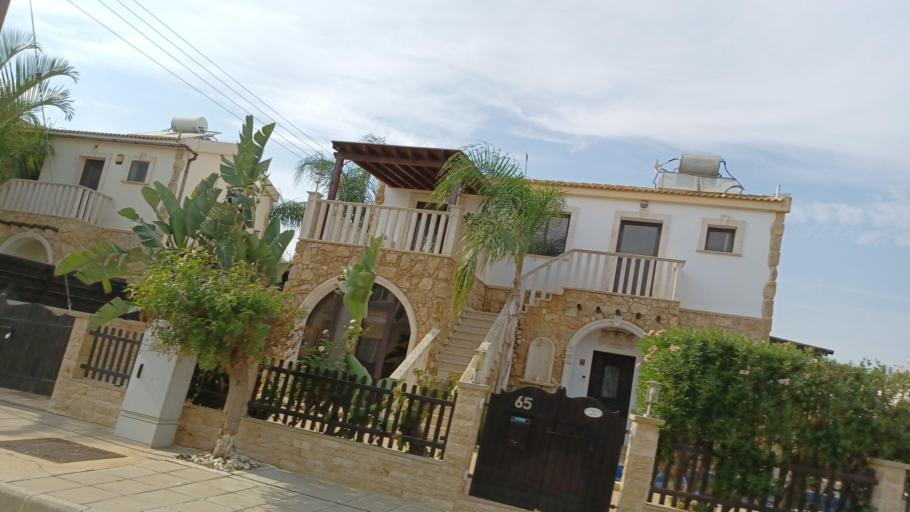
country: CY
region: Ammochostos
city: Frenaros
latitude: 35.0487
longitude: 33.9266
